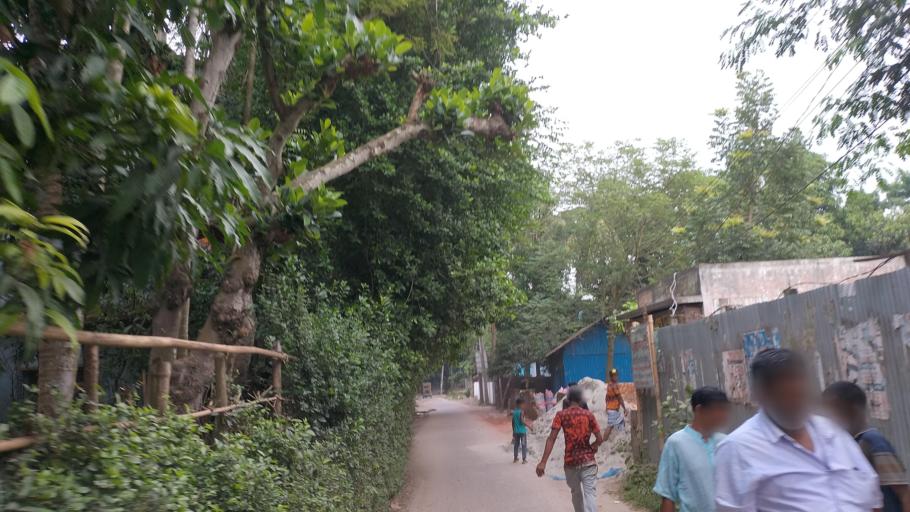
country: BD
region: Dhaka
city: Azimpur
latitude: 23.6845
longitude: 90.3099
